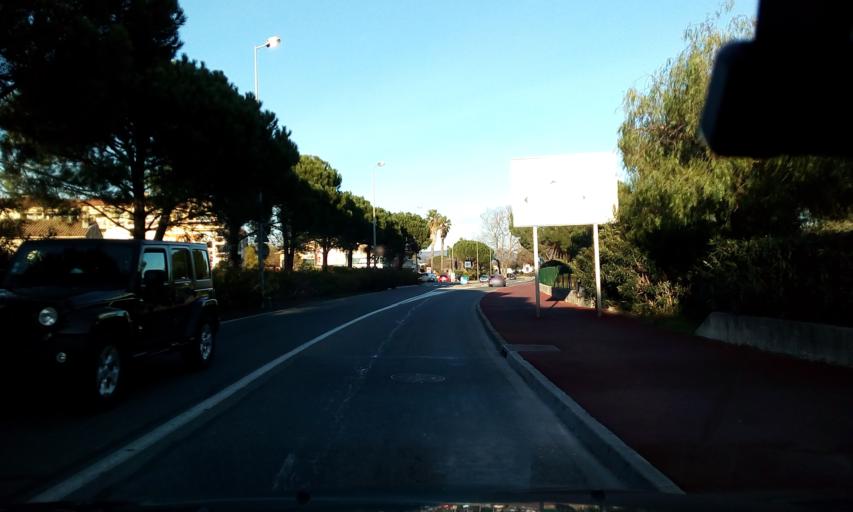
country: FR
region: Provence-Alpes-Cote d'Azur
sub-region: Departement du Var
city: Frejus
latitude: 43.4266
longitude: 6.7341
